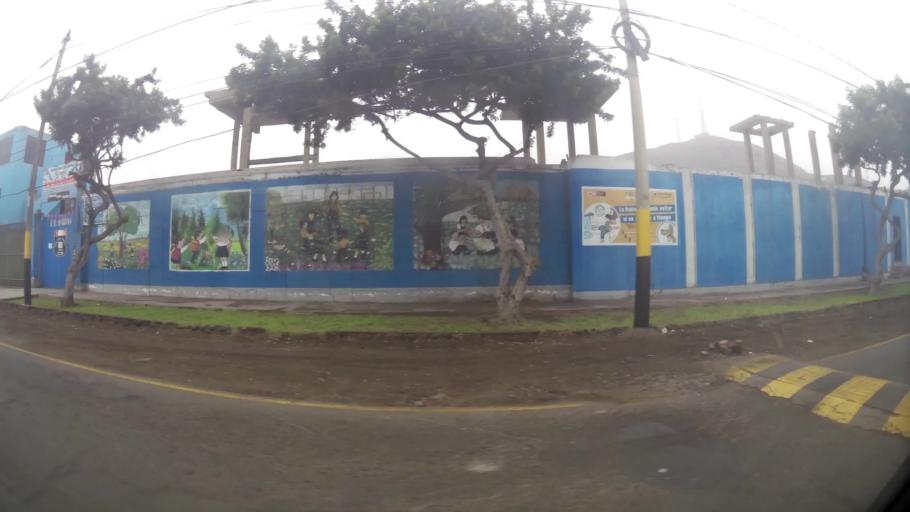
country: PE
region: Lima
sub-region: Provincia de Huaral
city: Chancay
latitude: -11.5812
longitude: -77.2692
